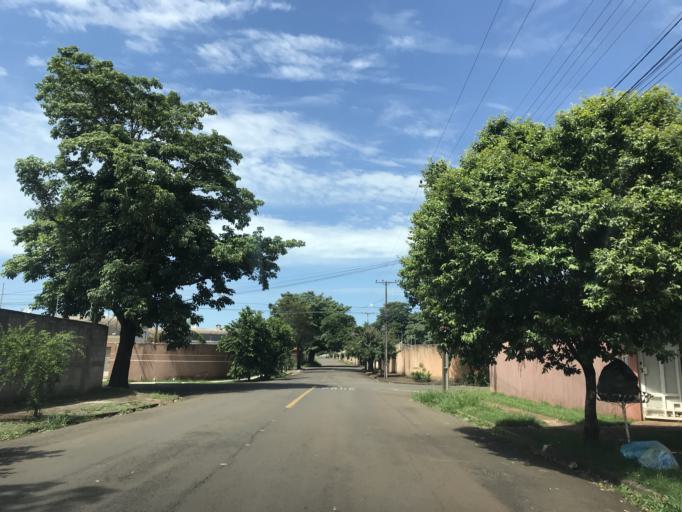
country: BR
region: Parana
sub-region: Londrina
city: Londrina
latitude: -23.3482
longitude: -51.1608
